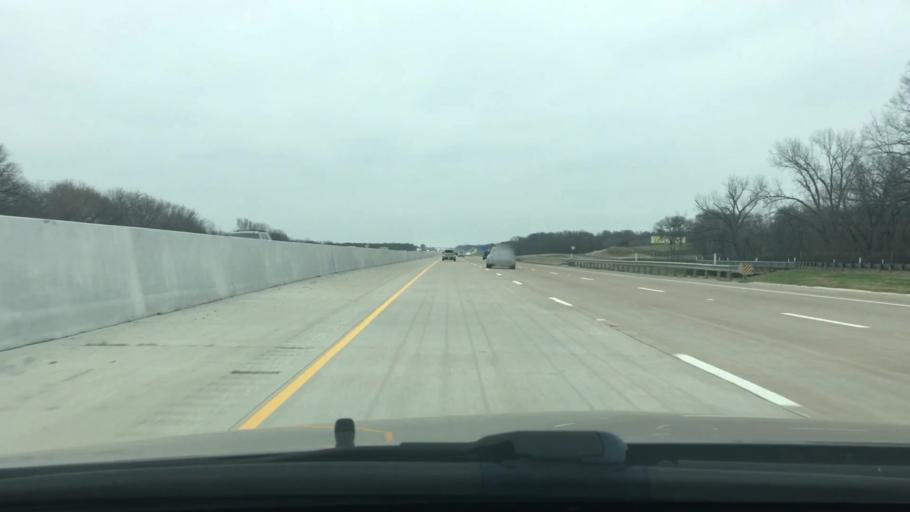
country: US
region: Texas
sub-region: Freestone County
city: Wortham
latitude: 31.9212
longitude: -96.4106
